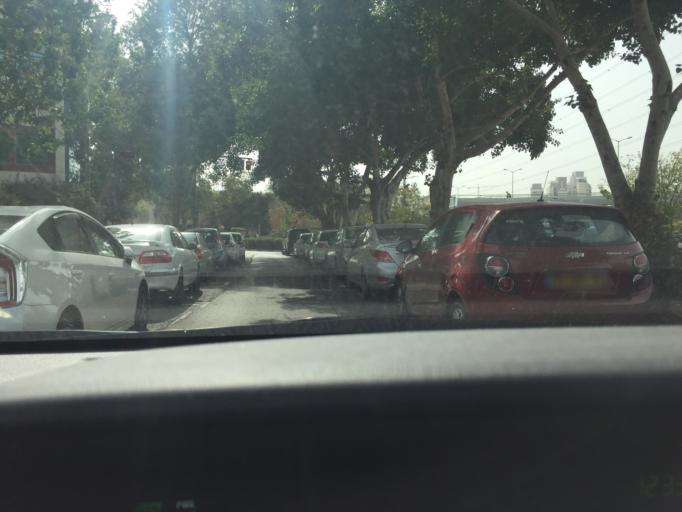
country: IL
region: Tel Aviv
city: Giv`at Shemu'el
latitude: 32.0678
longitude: 34.8408
